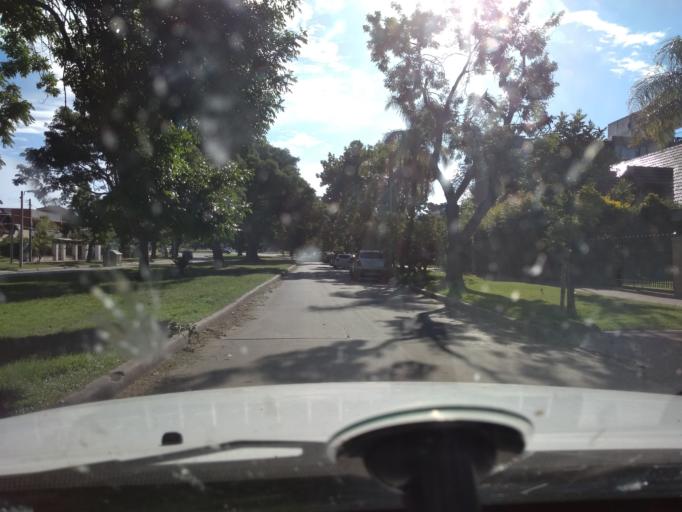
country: UY
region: Canelones
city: Paso de Carrasco
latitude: -34.8891
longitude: -56.0711
